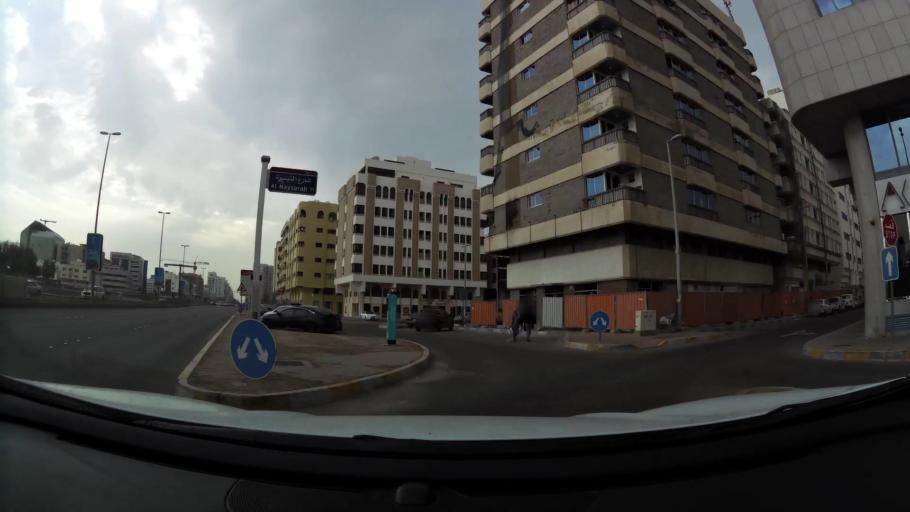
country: AE
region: Abu Dhabi
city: Abu Dhabi
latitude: 24.4884
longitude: 54.3829
